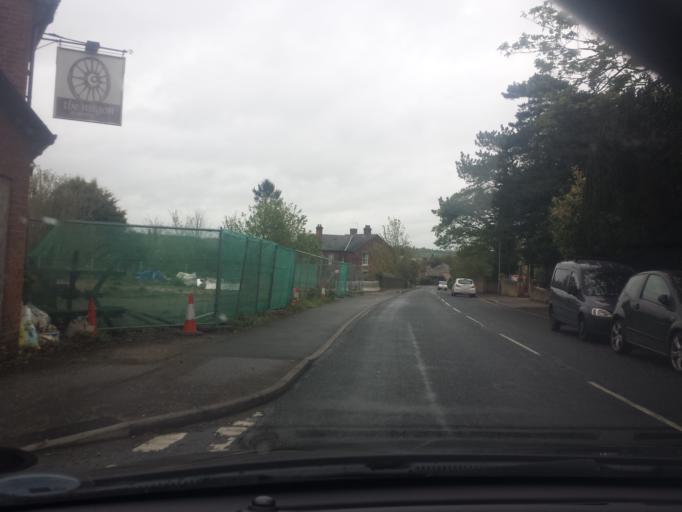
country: GB
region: England
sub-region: Essex
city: Manningtree
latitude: 51.9422
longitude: 1.0657
